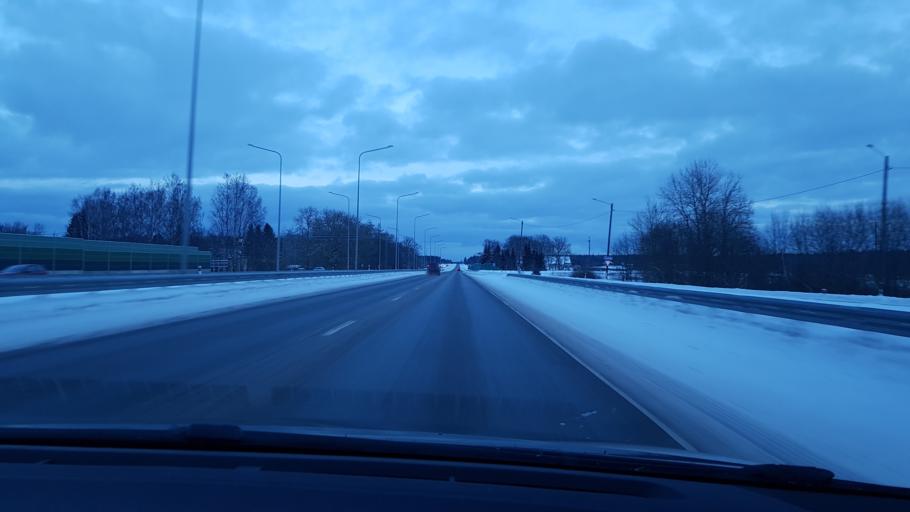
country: EE
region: Harju
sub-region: Kuusalu vald
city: Kuusalu
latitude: 59.4453
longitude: 25.3794
